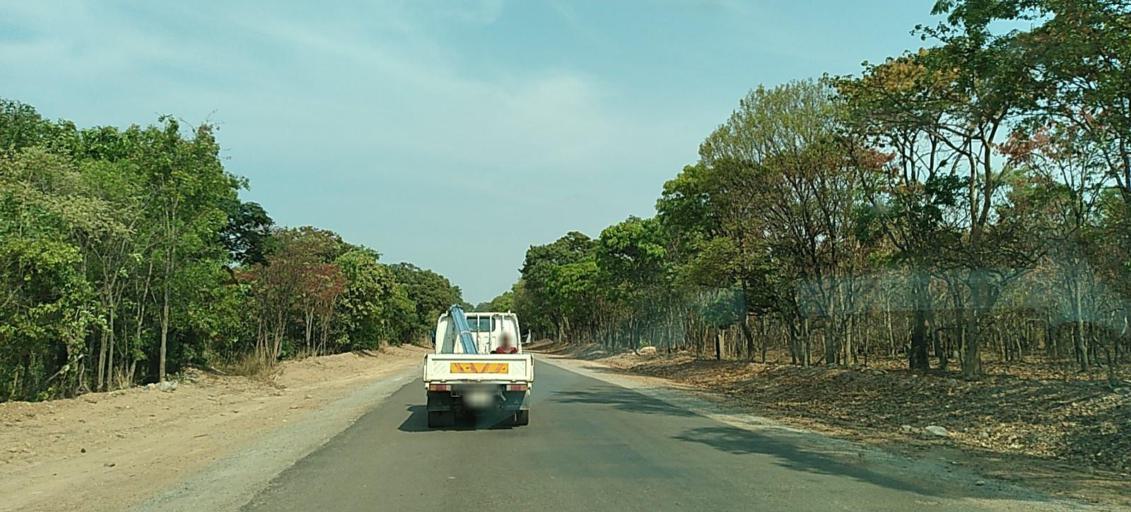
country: ZM
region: Copperbelt
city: Chililabombwe
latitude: -12.3062
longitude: 27.7875
